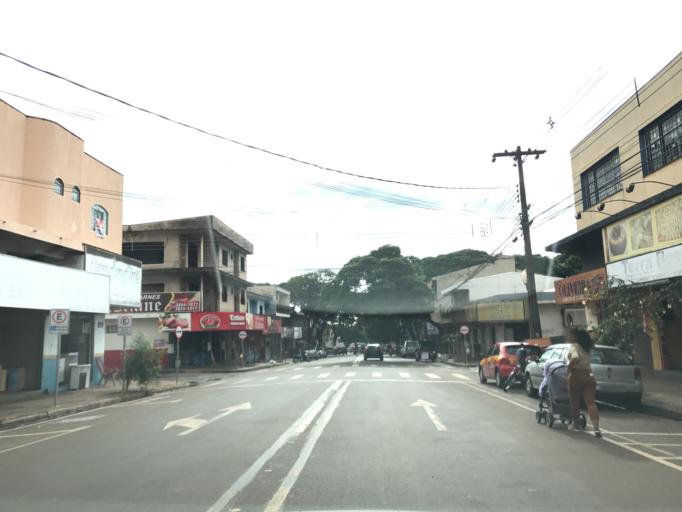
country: BR
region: Parana
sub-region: Sarandi
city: Sarandi
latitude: -23.4371
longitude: -51.8697
